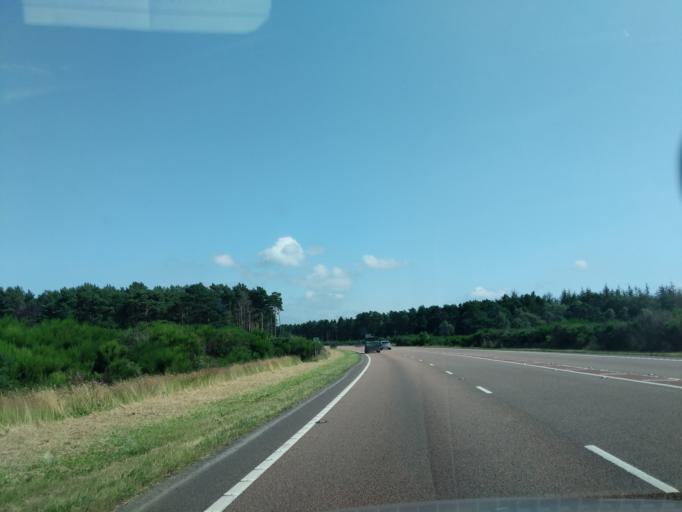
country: GB
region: Scotland
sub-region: Moray
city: Fochabers
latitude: 57.6250
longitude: -3.1397
